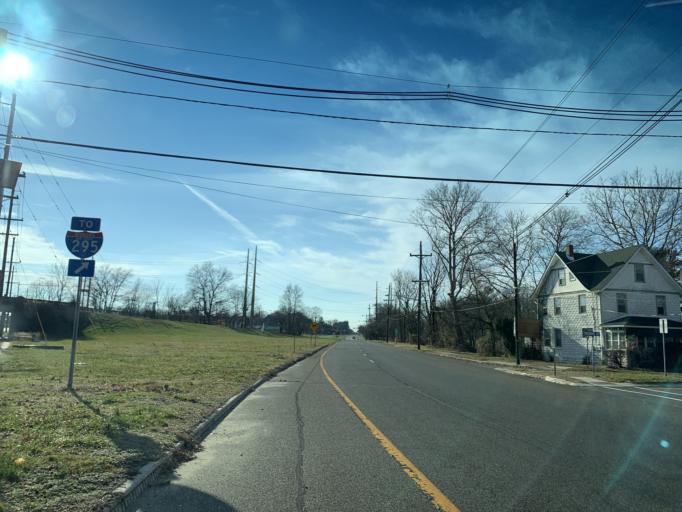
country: US
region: New Jersey
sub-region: Gloucester County
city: Westville
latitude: 39.8713
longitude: -75.1291
